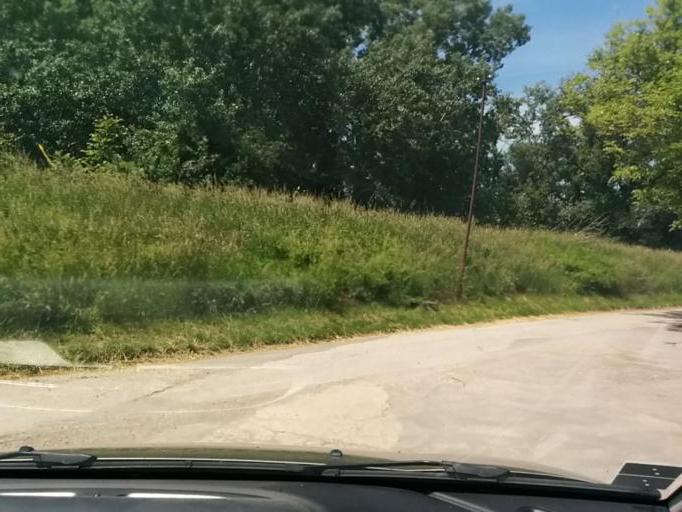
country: SK
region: Trnavsky
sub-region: Okres Galanta
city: Galanta
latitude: 48.2432
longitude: 17.8197
